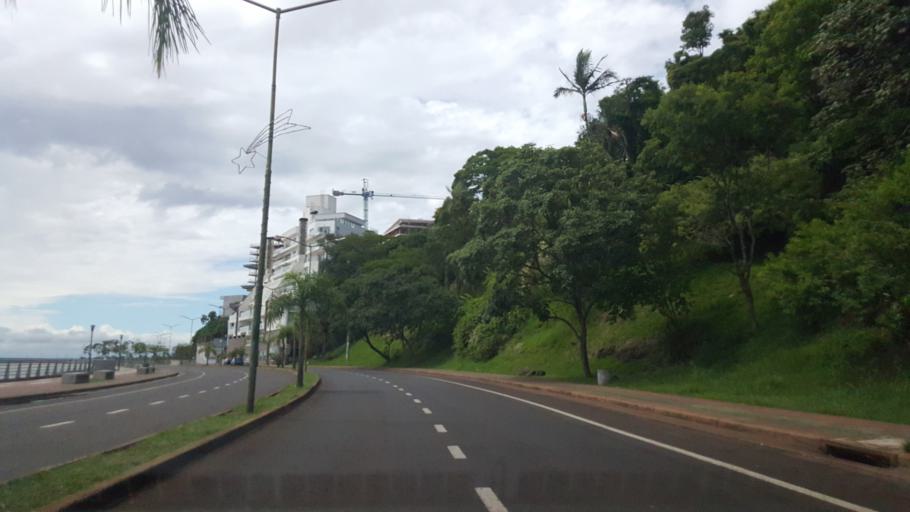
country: AR
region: Misiones
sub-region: Departamento de Capital
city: Posadas
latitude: -27.3544
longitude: -55.8925
